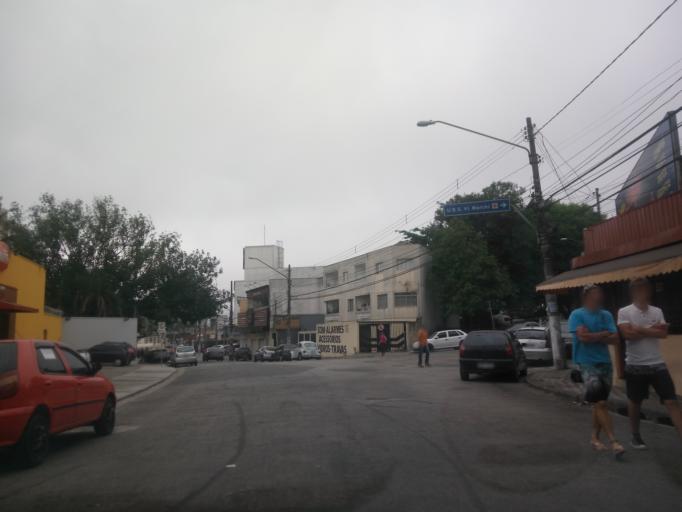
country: BR
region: Sao Paulo
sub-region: Sao Bernardo Do Campo
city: Sao Bernardo do Campo
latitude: -23.7212
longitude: -46.5642
